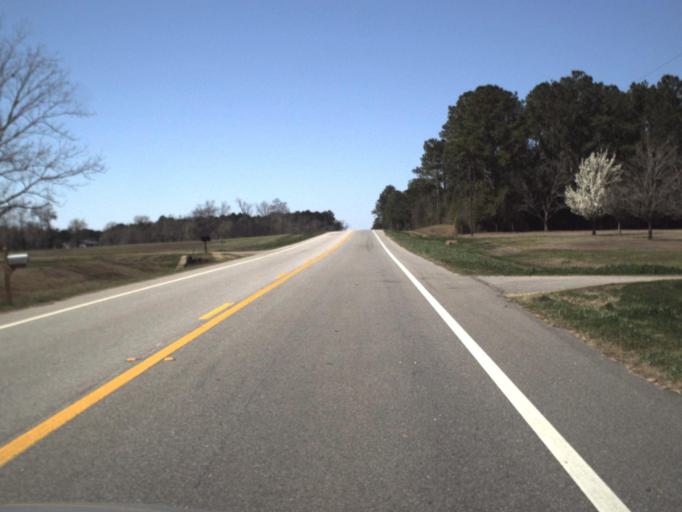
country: US
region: Florida
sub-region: Jackson County
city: Marianna
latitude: 30.8118
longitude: -85.3004
